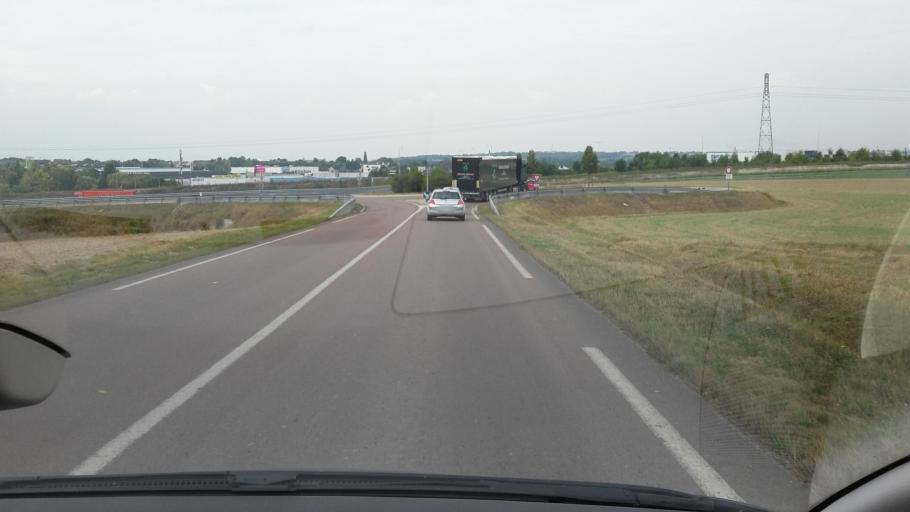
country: FR
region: Champagne-Ardenne
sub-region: Departement de la Marne
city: Cormontreuil
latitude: 49.2087
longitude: 4.0510
